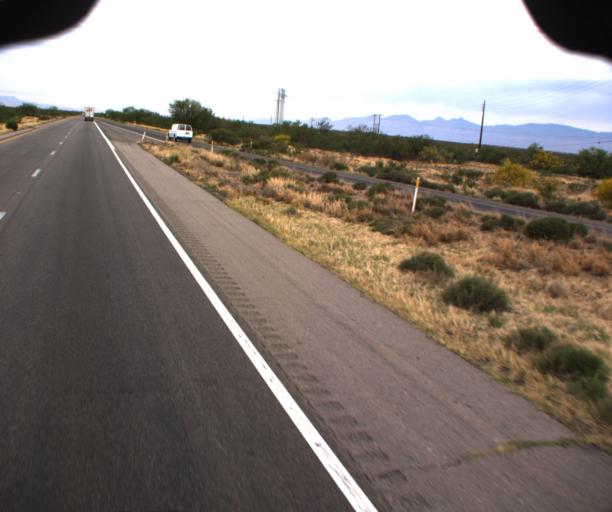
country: US
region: Arizona
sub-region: Pima County
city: Vail
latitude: 32.0296
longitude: -110.7221
